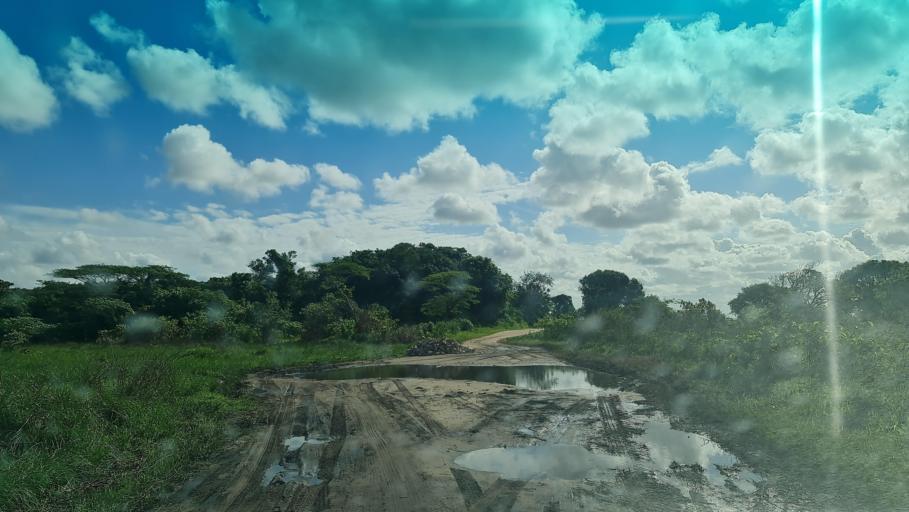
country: MZ
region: Maputo
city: Manhica
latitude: -25.4280
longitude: 32.8962
